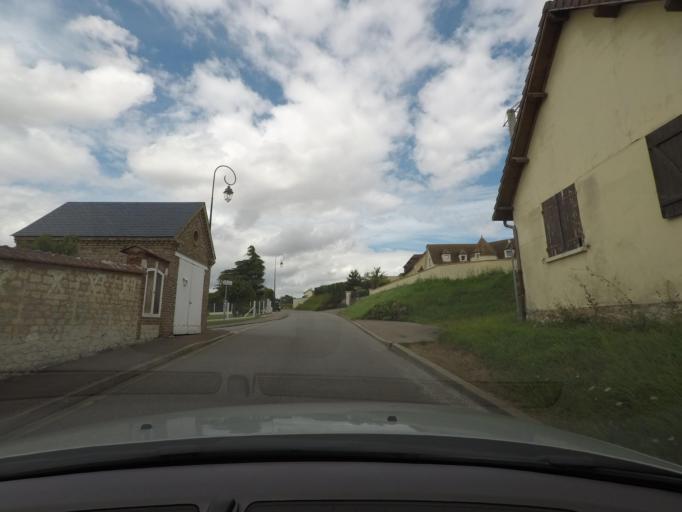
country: FR
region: Haute-Normandie
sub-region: Departement de l'Eure
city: Saint-Just
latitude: 49.1587
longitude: 1.4427
